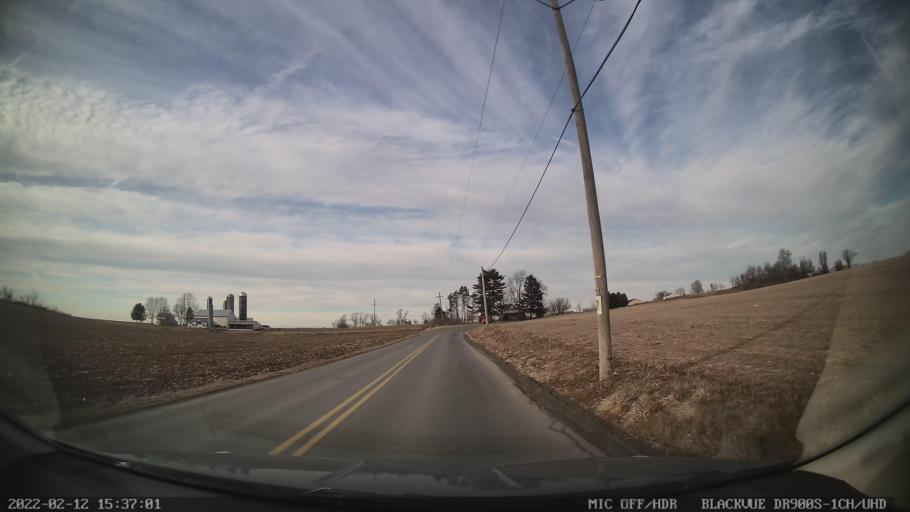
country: US
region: Pennsylvania
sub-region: Berks County
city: Topton
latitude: 40.4960
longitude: -75.7367
